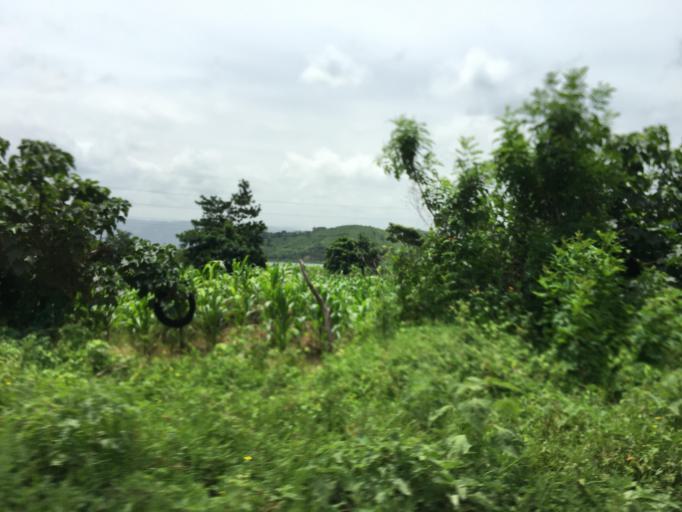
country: GT
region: Guatemala
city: Amatitlan
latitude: 14.4658
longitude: -90.5896
